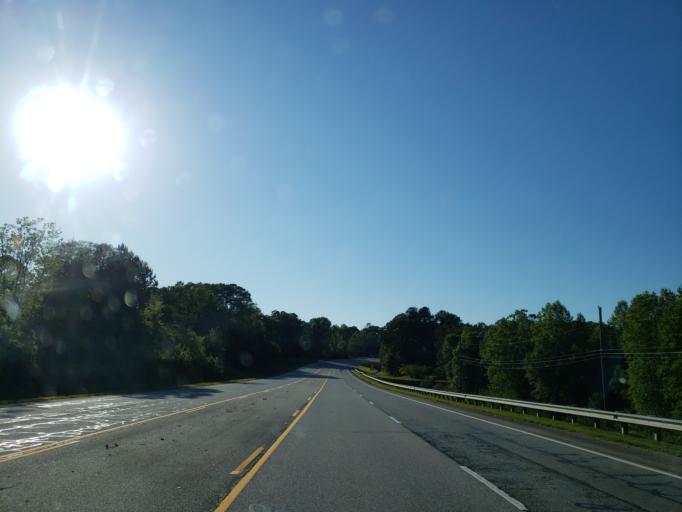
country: US
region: Georgia
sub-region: Haralson County
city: Buchanan
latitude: 33.8851
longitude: -85.2201
